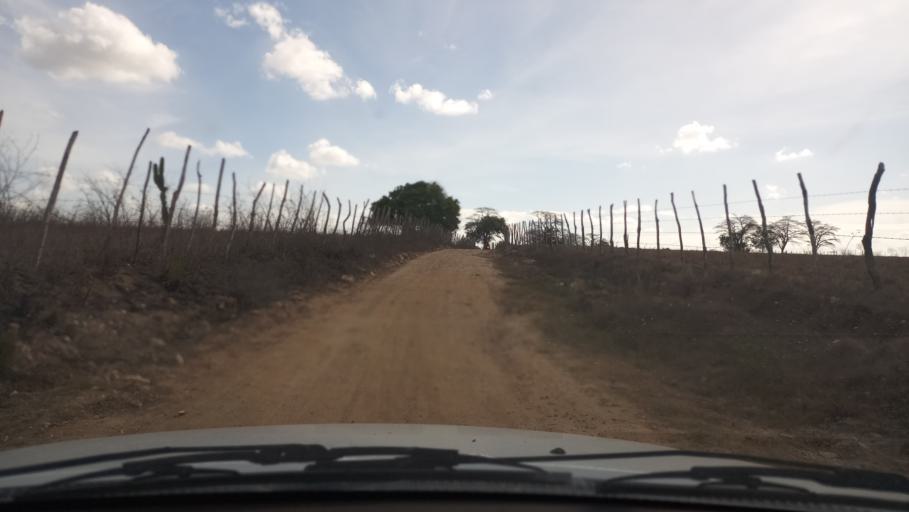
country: BR
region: Rio Grande do Norte
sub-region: Goianinha
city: Goianinha
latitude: -6.3136
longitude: -35.3068
